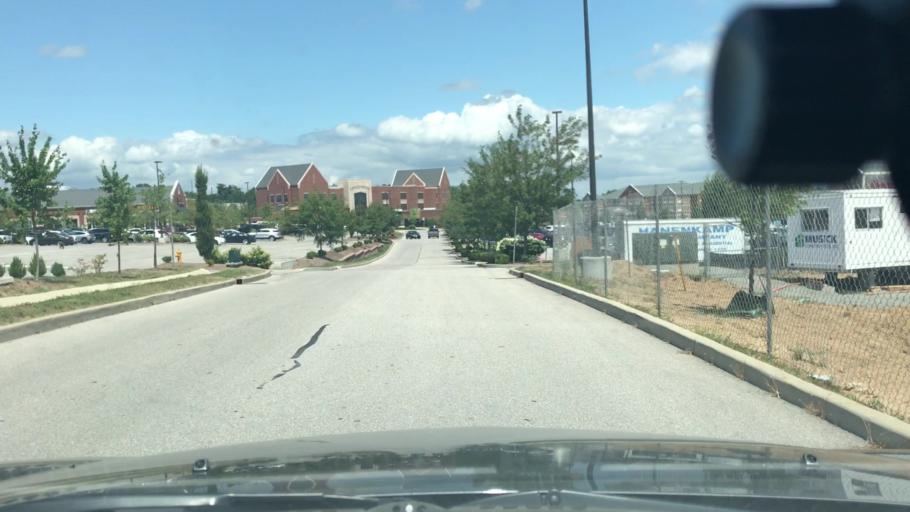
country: US
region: Missouri
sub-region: Saint Charles County
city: Saint Charles
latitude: 38.7822
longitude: -90.5035
